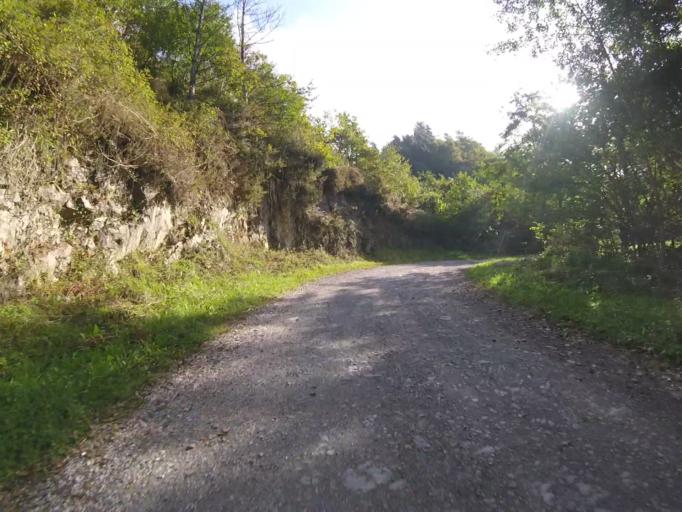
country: ES
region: Basque Country
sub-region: Provincia de Guipuzcoa
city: Elduayen
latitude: 43.1776
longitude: -1.9889
